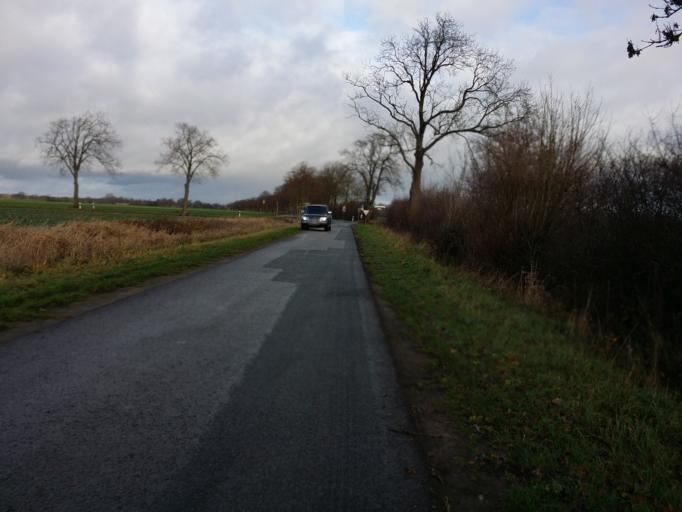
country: DE
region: Lower Saxony
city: Riede
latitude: 52.9874
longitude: 8.9781
